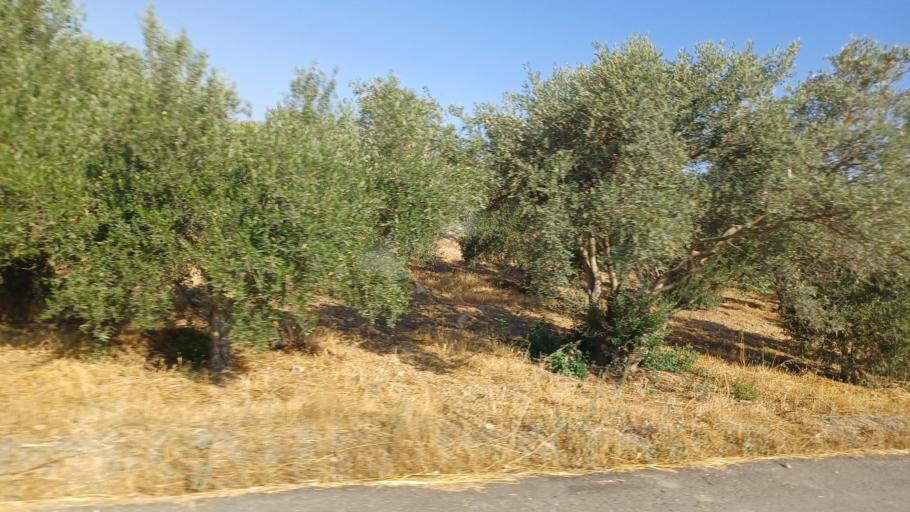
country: CY
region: Larnaka
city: Athienou
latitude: 35.0655
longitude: 33.5203
